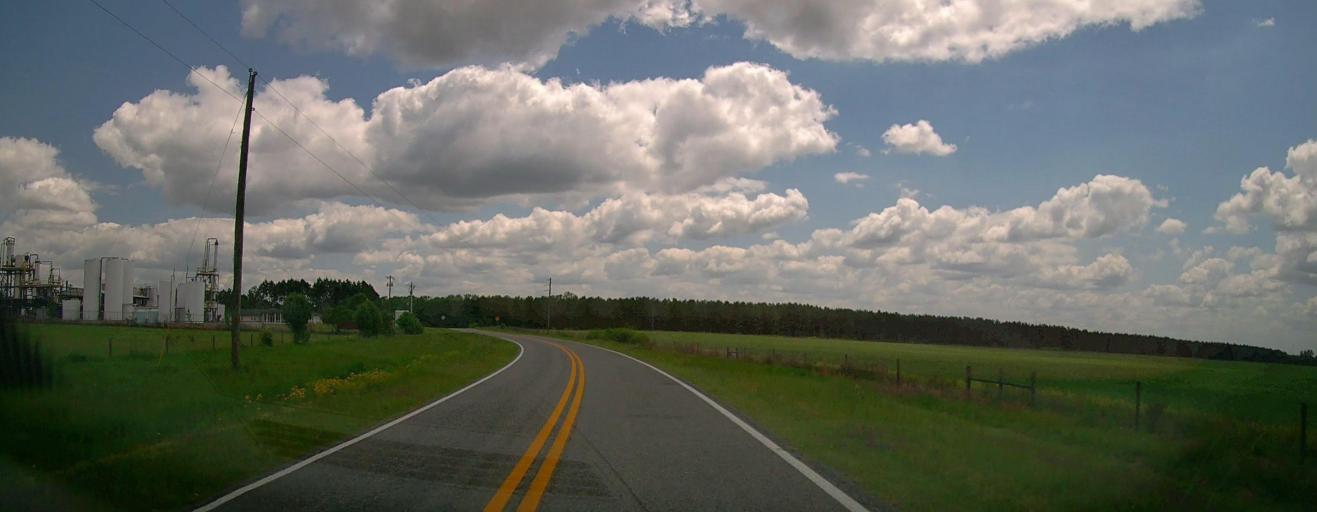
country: US
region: Georgia
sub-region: Laurens County
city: East Dublin
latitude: 32.5447
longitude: -82.8186
